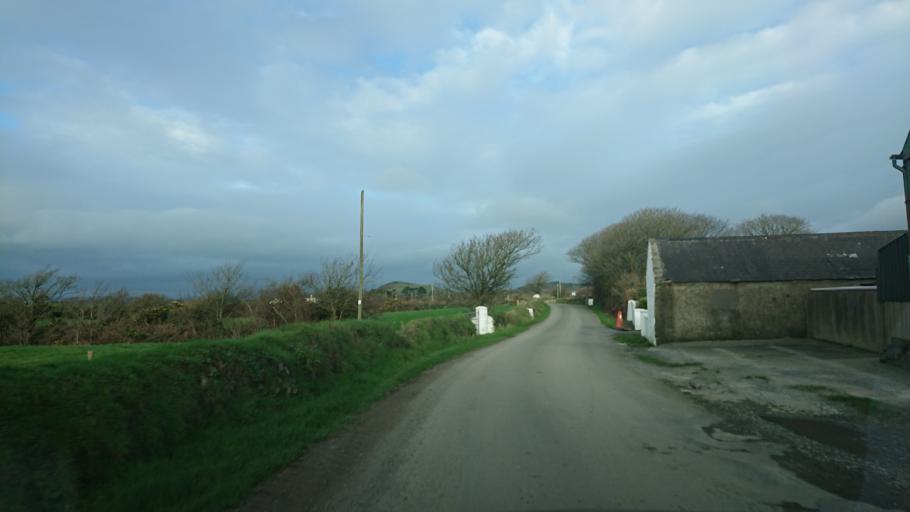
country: IE
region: Munster
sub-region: Waterford
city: Tra Mhor
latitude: 52.1499
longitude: -7.2123
